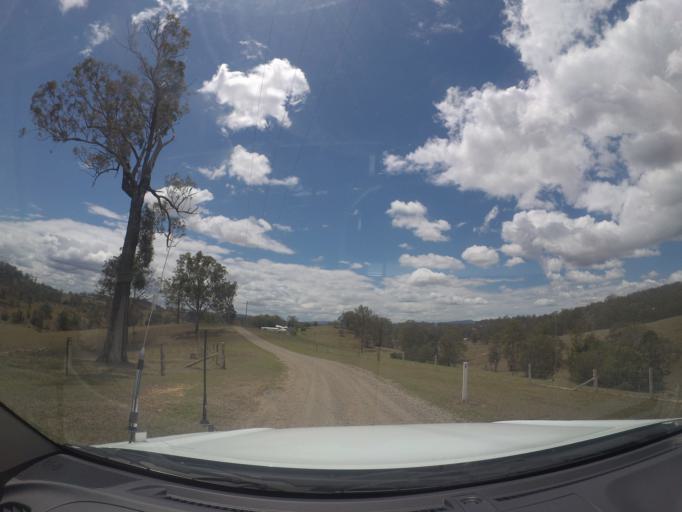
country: AU
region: Queensland
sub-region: Logan
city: Cedar Vale
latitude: -27.9081
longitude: 153.0566
